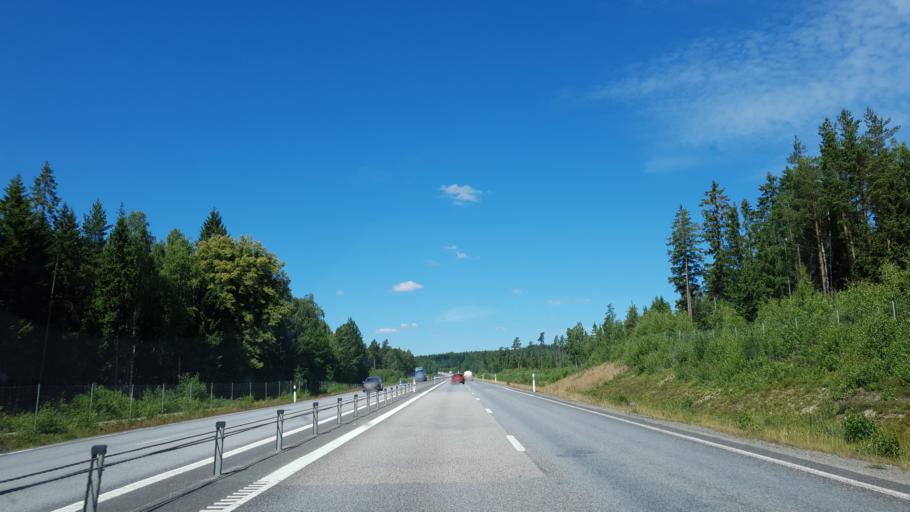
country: SE
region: Kronoberg
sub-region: Vaxjo Kommun
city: Gemla
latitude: 56.9142
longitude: 14.6269
